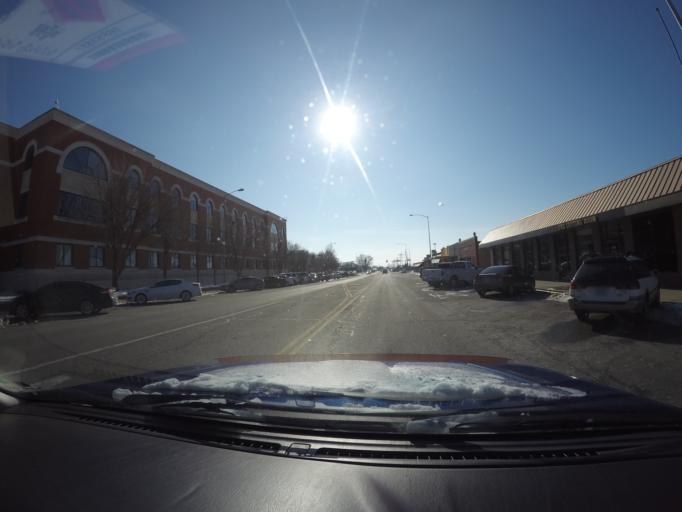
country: US
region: Kansas
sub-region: Johnson County
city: Olathe
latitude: 38.8819
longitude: -94.8207
